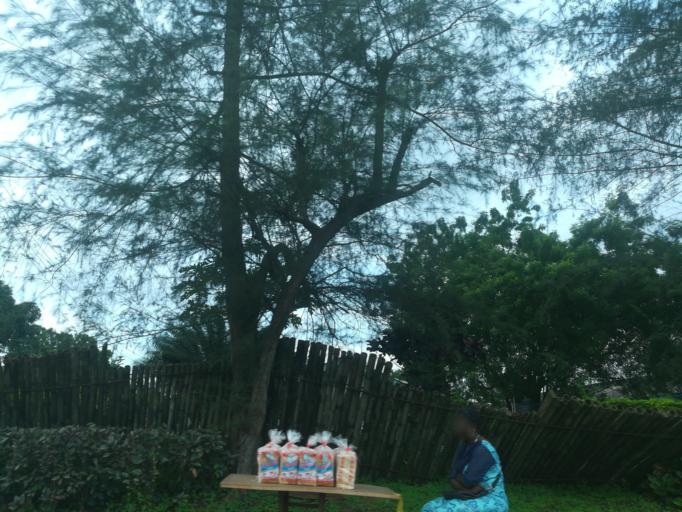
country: NG
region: Lagos
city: Ikorodu
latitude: 6.6448
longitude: 3.5225
